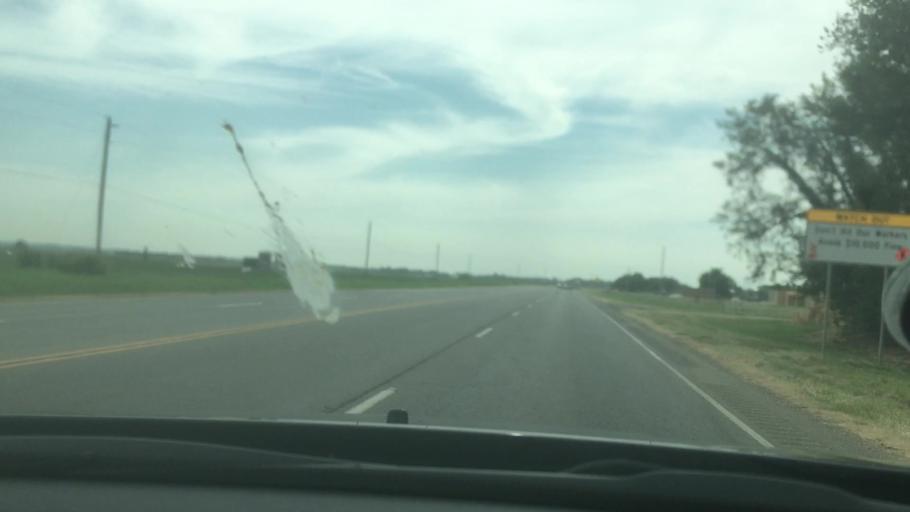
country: US
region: Oklahoma
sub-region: Garvin County
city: Lindsay
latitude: 34.8358
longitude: -97.5902
